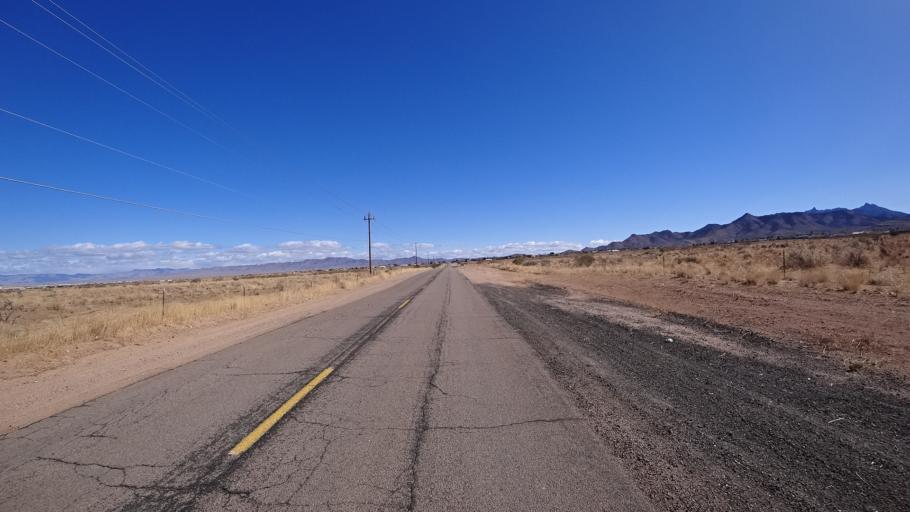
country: US
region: Arizona
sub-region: Mohave County
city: Kingman
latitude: 35.2001
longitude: -113.9885
